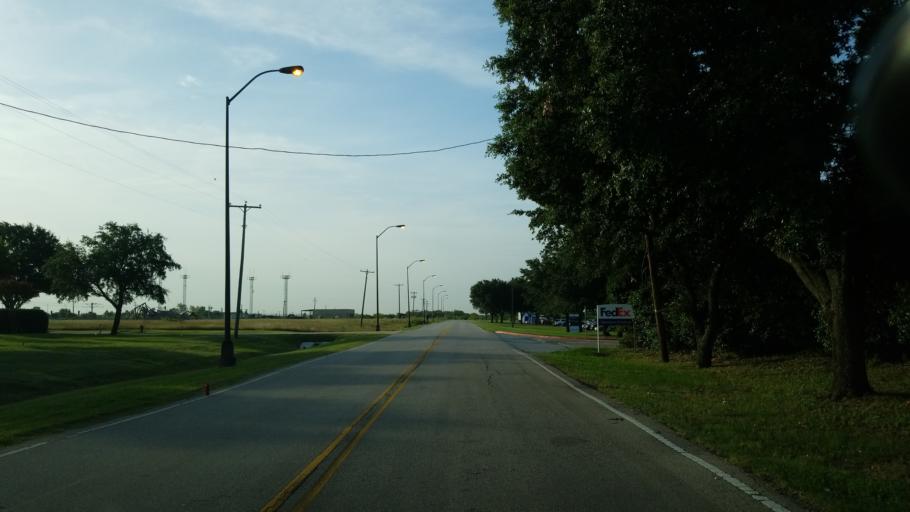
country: US
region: Texas
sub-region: Dallas County
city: Coppell
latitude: 32.9149
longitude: -97.0175
